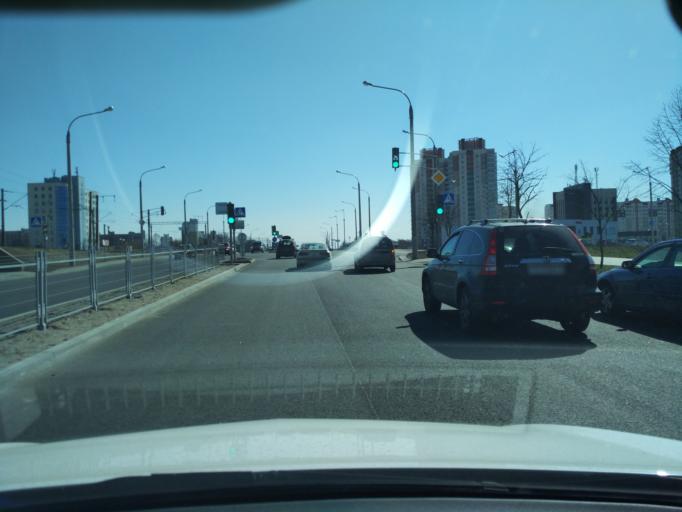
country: BY
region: Minsk
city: Minsk
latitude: 53.8738
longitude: 27.5615
